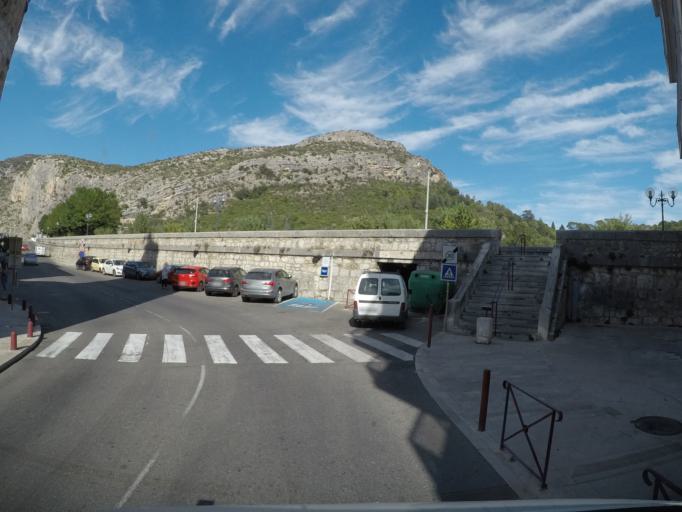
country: FR
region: Languedoc-Roussillon
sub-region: Departement du Gard
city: Anduze
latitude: 44.0539
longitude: 3.9872
